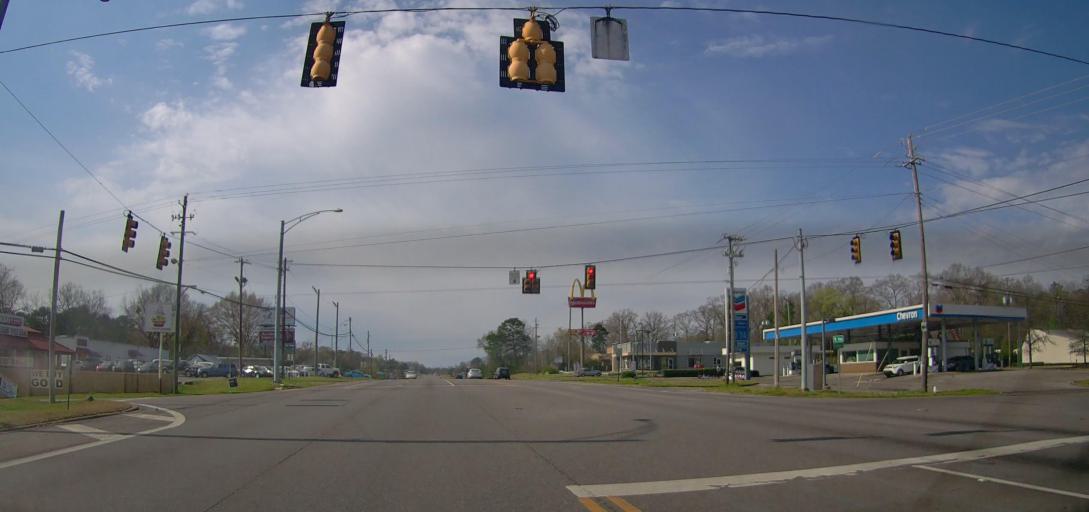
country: US
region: Alabama
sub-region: Jefferson County
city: Forestdale
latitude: 33.5606
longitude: -86.8923
